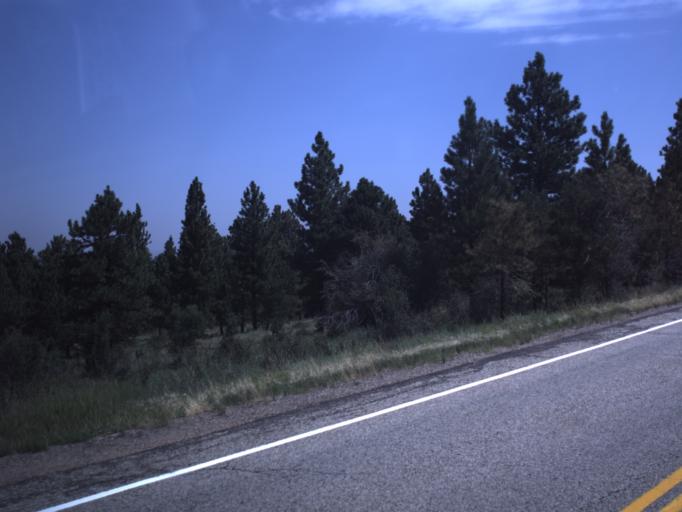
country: US
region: Utah
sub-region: Daggett County
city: Manila
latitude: 40.8629
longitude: -109.5262
